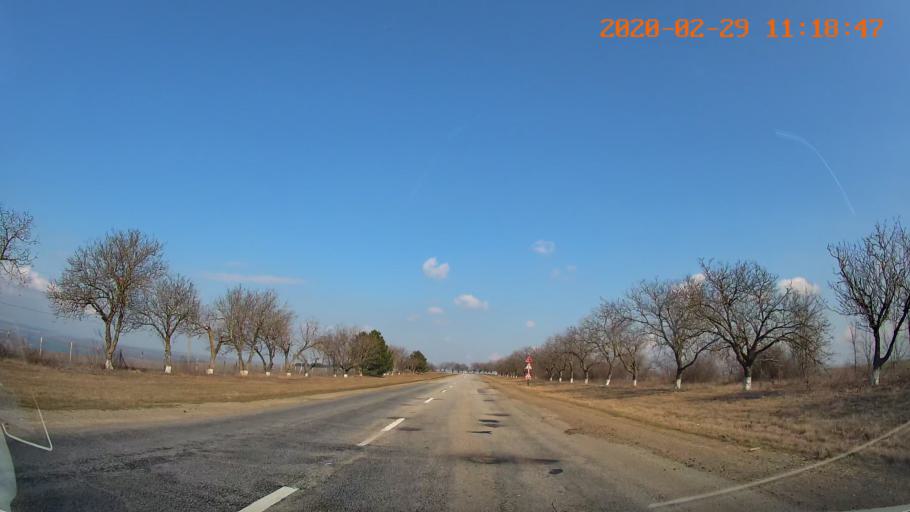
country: MD
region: Telenesti
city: Cocieri
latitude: 47.3400
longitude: 29.1751
